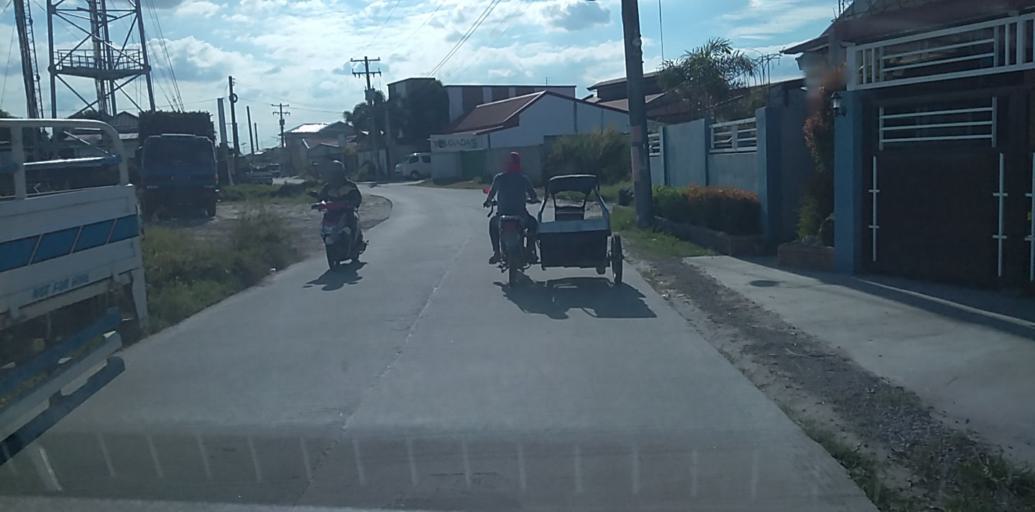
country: PH
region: Central Luzon
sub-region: Province of Pampanga
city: Acli
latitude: 15.1162
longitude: 120.6407
